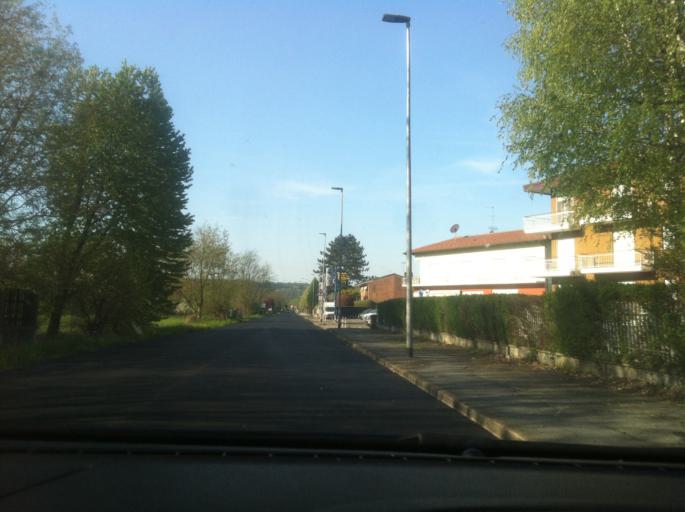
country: IT
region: Piedmont
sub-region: Provincia di Torino
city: Strambino
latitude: 45.3768
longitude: 7.8820
